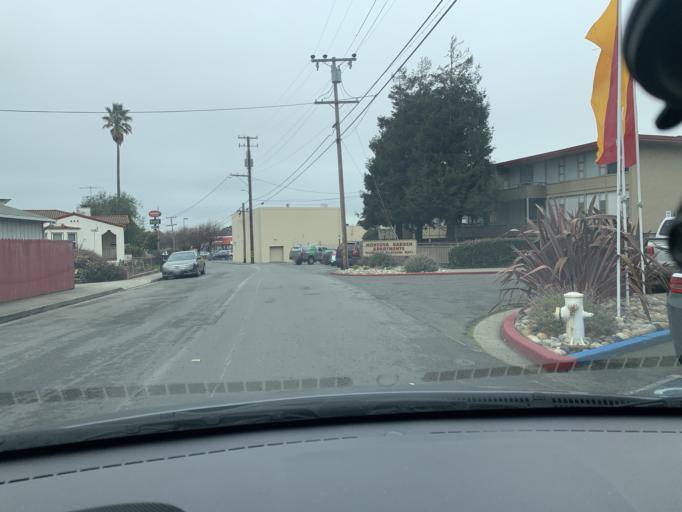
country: US
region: California
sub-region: Contra Costa County
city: Rollingwood
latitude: 37.9498
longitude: -122.3298
